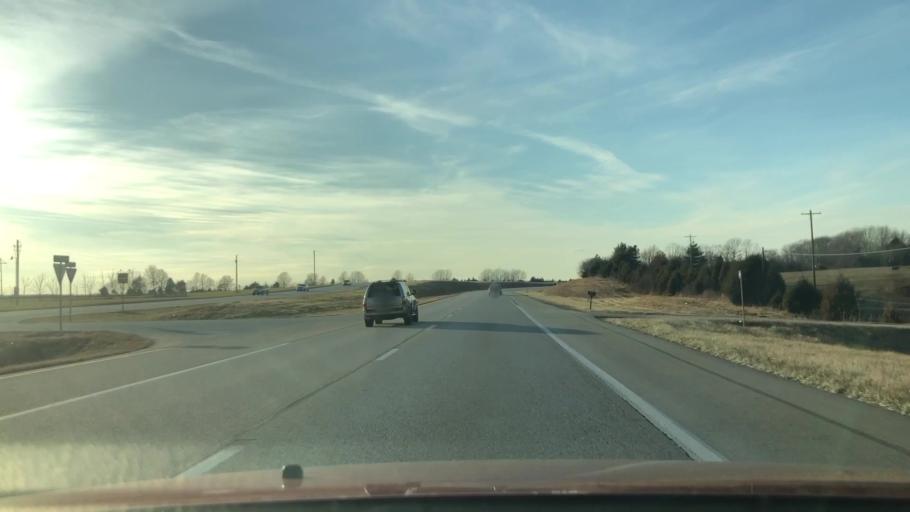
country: US
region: Missouri
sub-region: Webster County
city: Seymour
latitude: 37.1187
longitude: -92.6880
